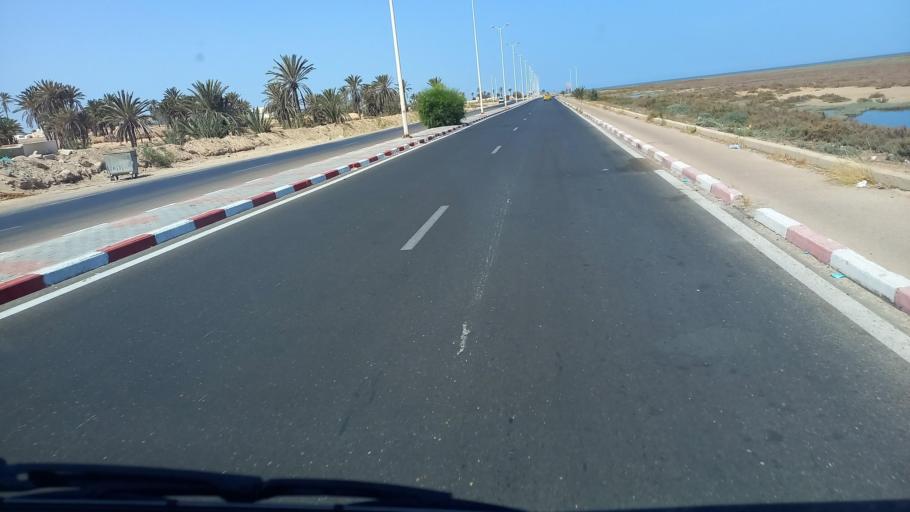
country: TN
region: Madanin
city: Houmt Souk
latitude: 33.8727
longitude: 10.9325
